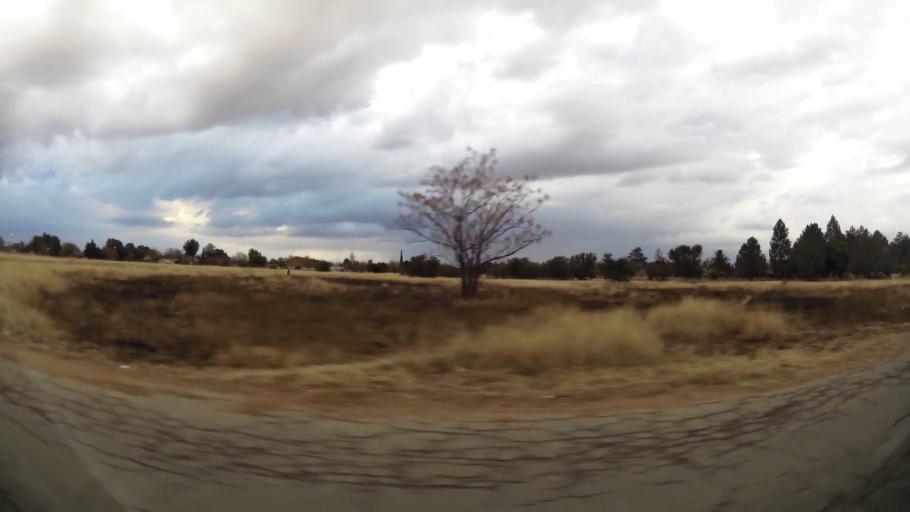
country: ZA
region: Orange Free State
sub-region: Lejweleputswa District Municipality
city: Welkom
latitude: -27.9677
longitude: 26.7234
